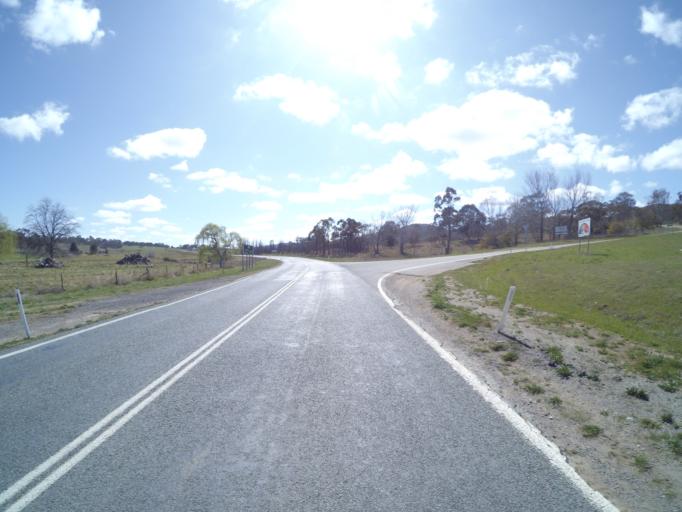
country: AU
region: New South Wales
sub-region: Queanbeyan
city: Queanbeyan
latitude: -35.3199
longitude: 149.2433
